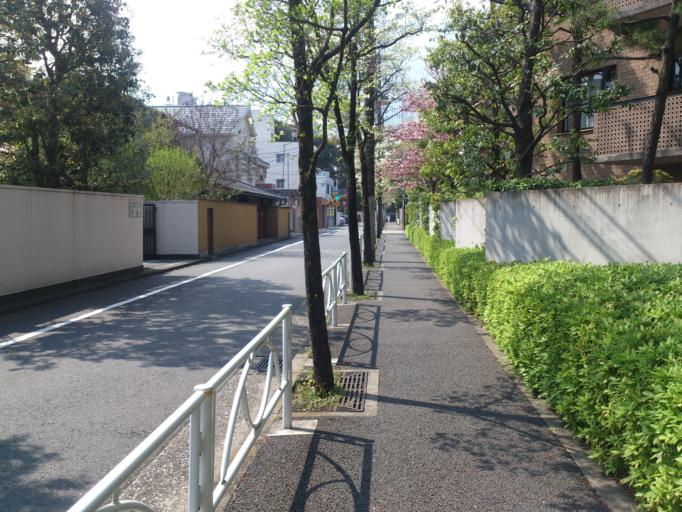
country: JP
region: Tokyo
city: Tokyo
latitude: 35.6601
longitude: 139.6802
